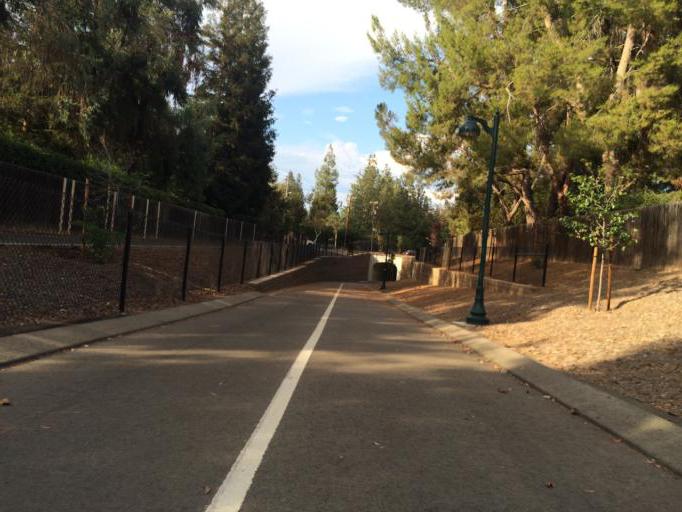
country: US
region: California
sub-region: Fresno County
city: Clovis
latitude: 36.8657
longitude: -119.7688
